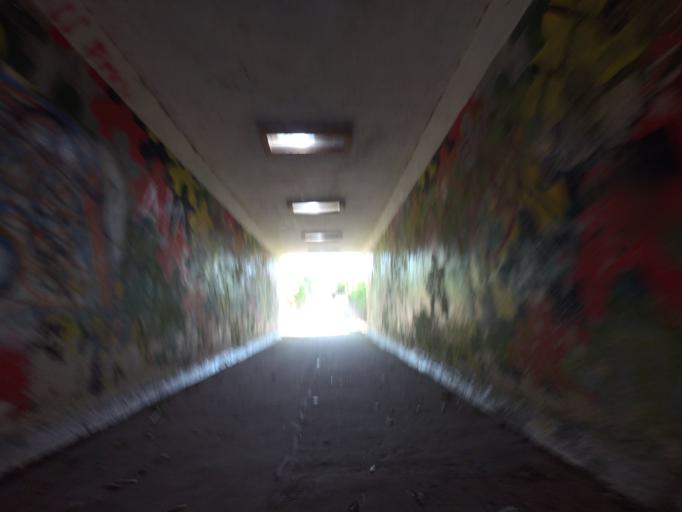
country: GB
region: Scotland
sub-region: Highland
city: Tain
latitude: 57.8066
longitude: -4.0656
